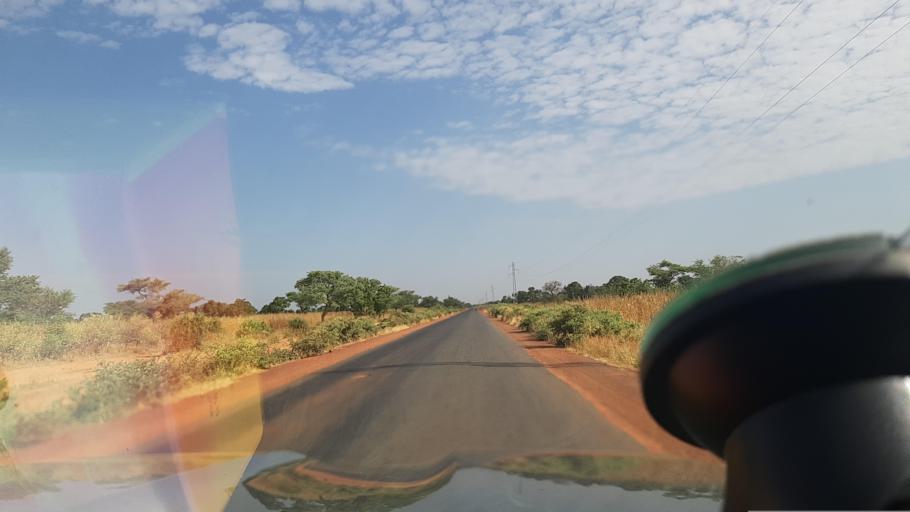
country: ML
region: Segou
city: Markala
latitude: 13.5544
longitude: -6.1150
